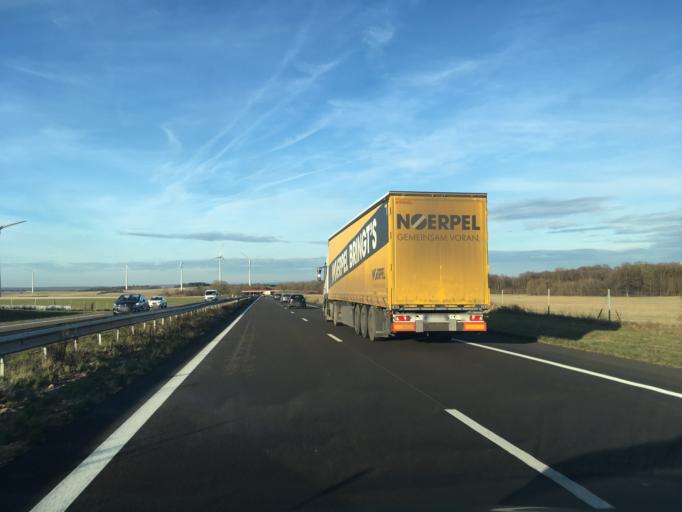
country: FR
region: Bourgogne
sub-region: Departement de l'Yonne
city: Joux-la-Ville
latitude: 47.6216
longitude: 3.9083
